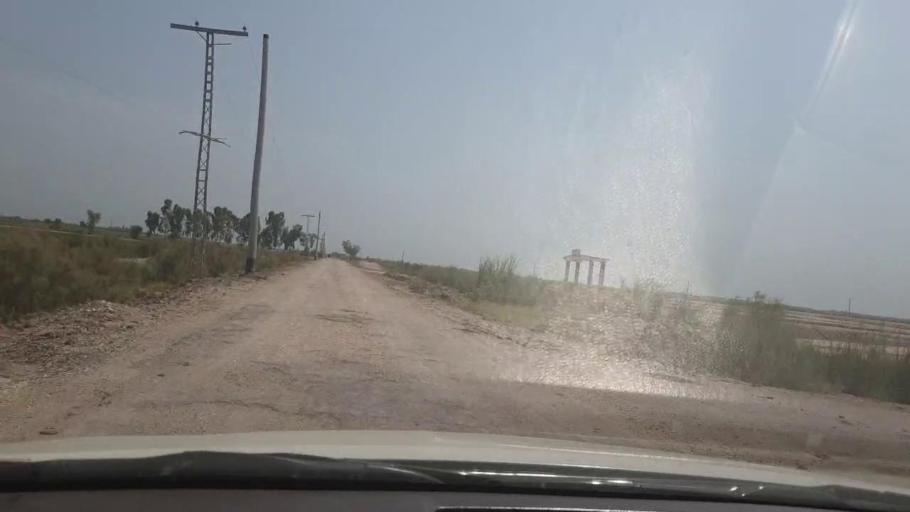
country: PK
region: Sindh
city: Garhi Yasin
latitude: 27.9586
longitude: 68.5051
